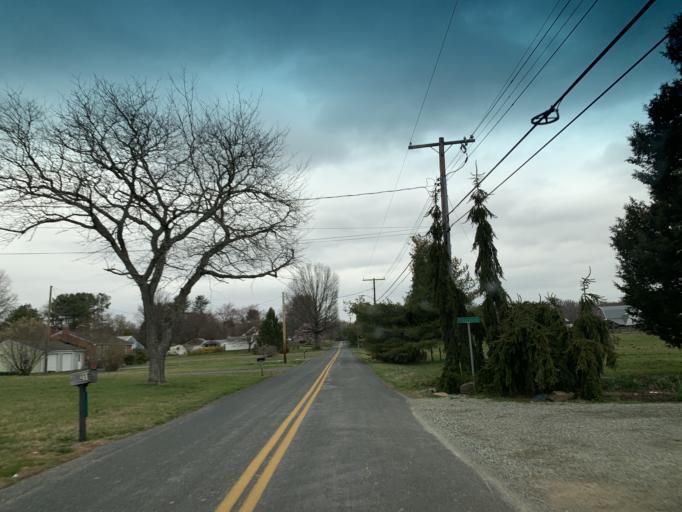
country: US
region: Maryland
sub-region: Harford County
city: Aberdeen
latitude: 39.5725
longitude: -76.1975
